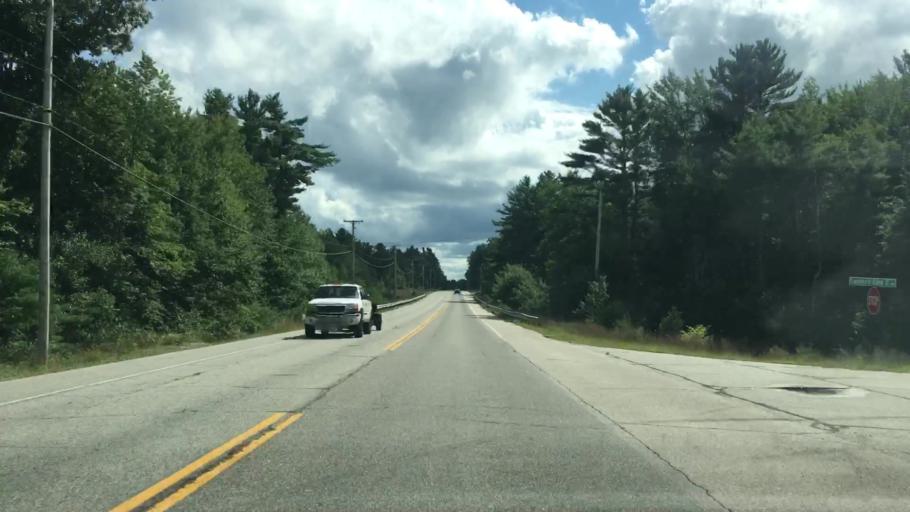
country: US
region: Maine
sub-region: York County
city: South Sanford
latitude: 43.3881
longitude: -70.7399
